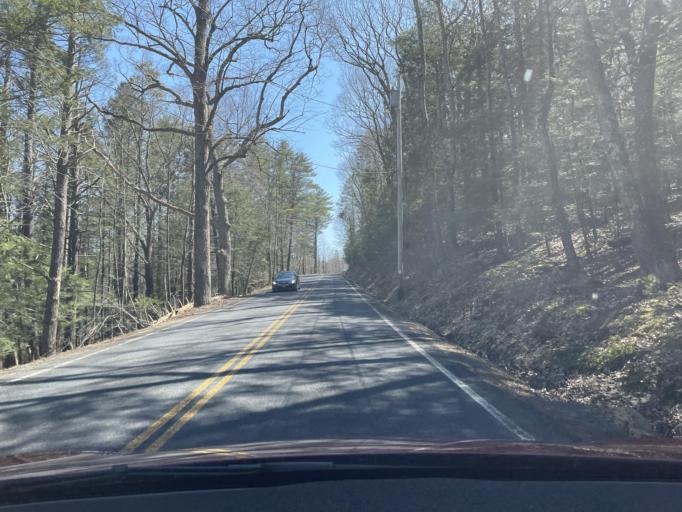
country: US
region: New York
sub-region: Ulster County
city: Woodstock
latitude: 42.0095
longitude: -74.1644
